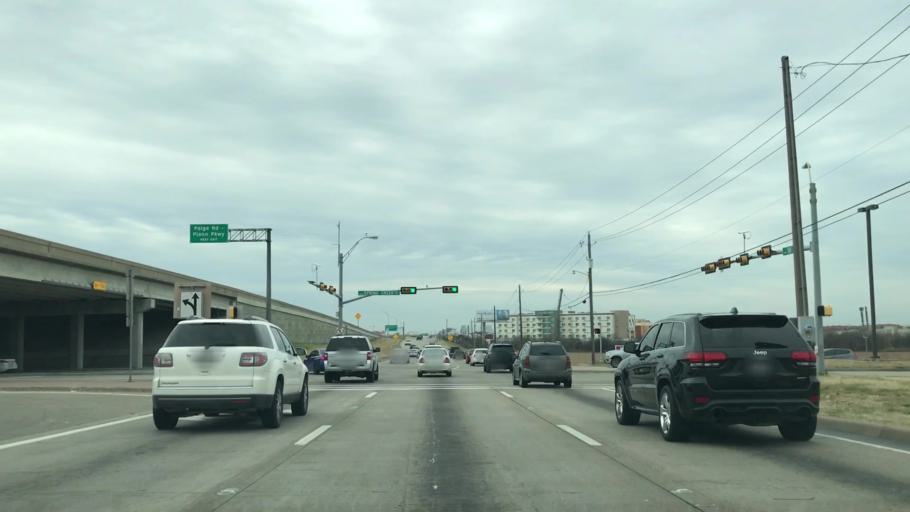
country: US
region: Texas
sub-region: Denton County
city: The Colony
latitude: 33.0831
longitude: -96.8520
